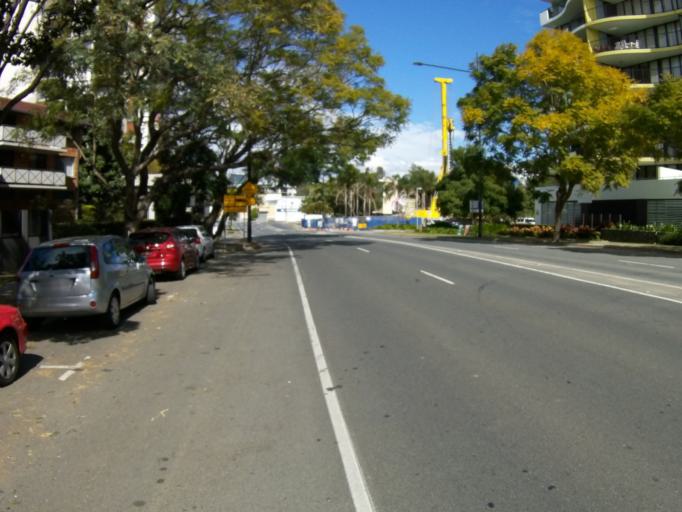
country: AU
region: Queensland
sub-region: Brisbane
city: Toowong
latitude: -27.4807
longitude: 152.9958
